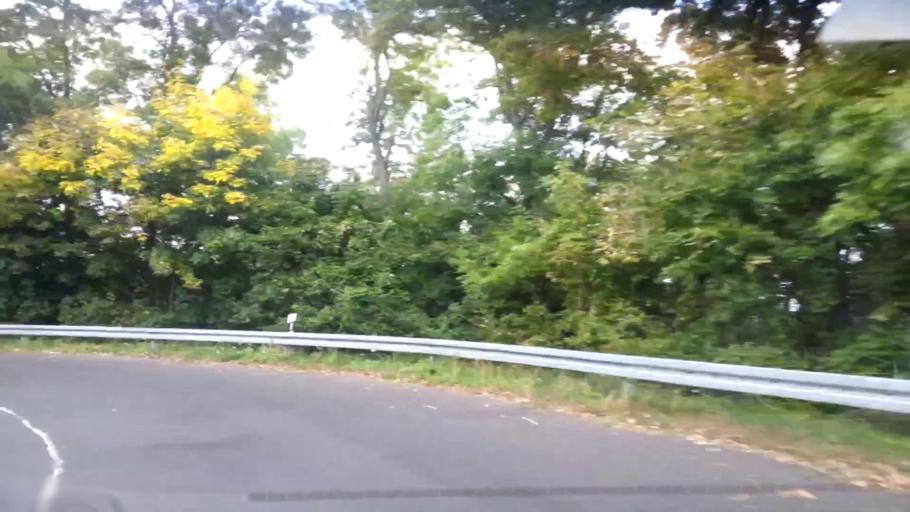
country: DE
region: Bavaria
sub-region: Regierungsbezirk Unterfranken
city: Rodelsee
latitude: 49.7279
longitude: 10.2689
